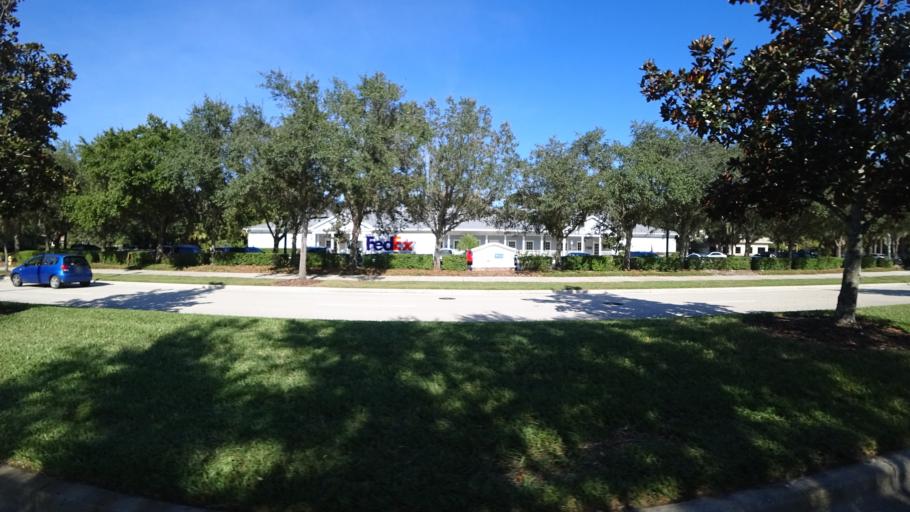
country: US
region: Florida
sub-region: Sarasota County
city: The Meadows
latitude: 27.3941
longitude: -82.4466
